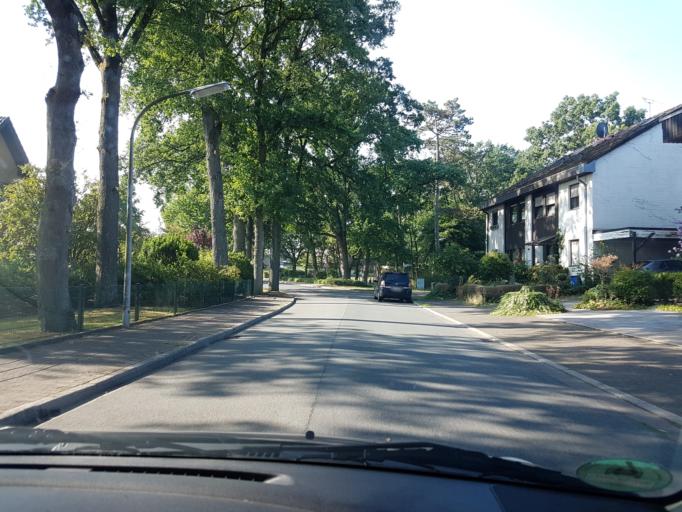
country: DE
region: North Rhine-Westphalia
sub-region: Regierungsbezirk Munster
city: Heiden
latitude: 51.7583
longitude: 6.9542
